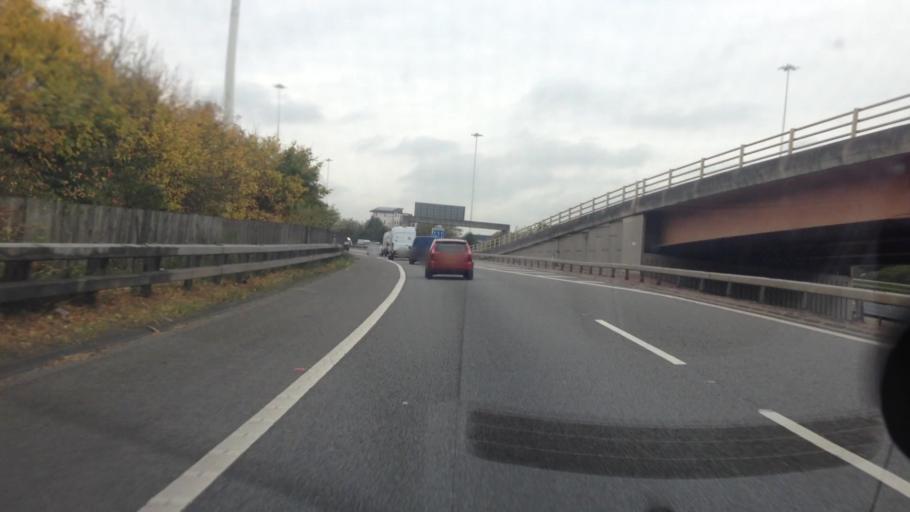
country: GB
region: England
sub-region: City and Borough of Leeds
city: Leeds
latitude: 53.7846
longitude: -1.5484
